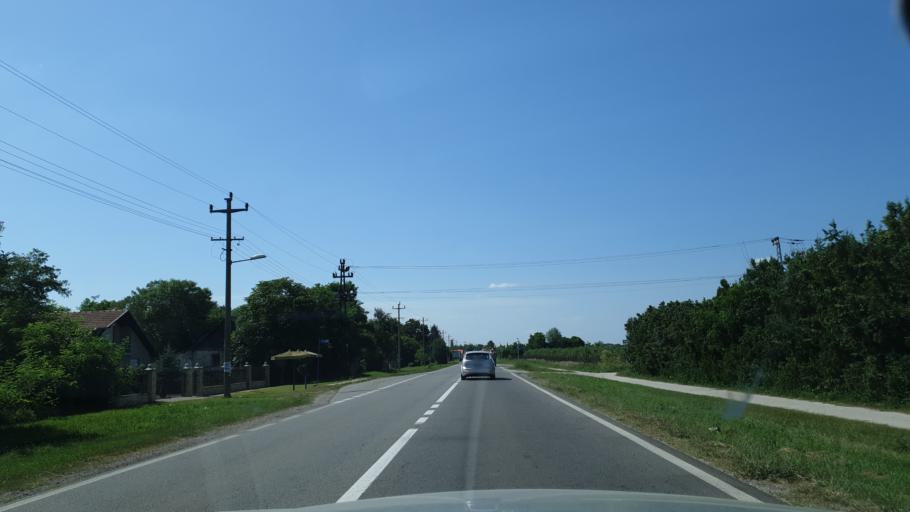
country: HU
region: Bacs-Kiskun
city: Kelebia
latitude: 46.1371
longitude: 19.5948
